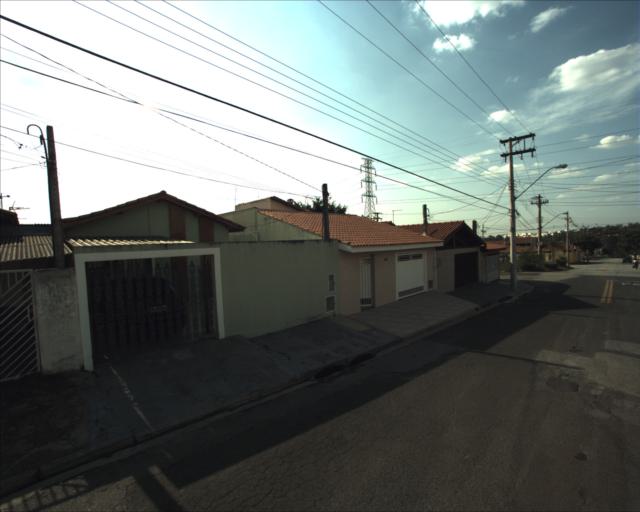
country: BR
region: Sao Paulo
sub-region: Sorocaba
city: Sorocaba
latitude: -23.4939
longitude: -47.5208
